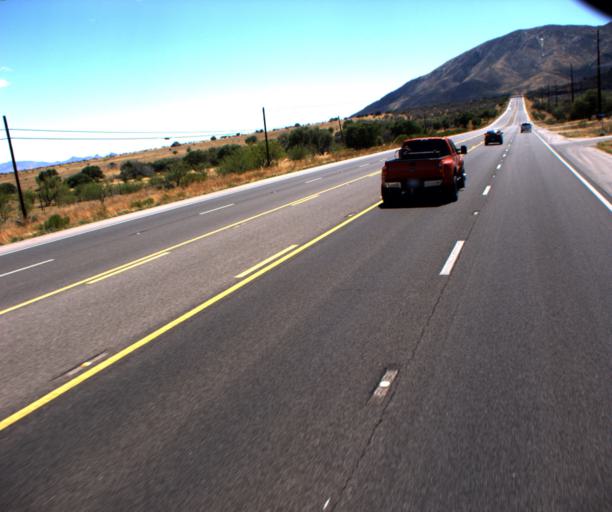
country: US
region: Arizona
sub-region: Cochise County
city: Sierra Vista Southeast
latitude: 31.4208
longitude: -110.2408
